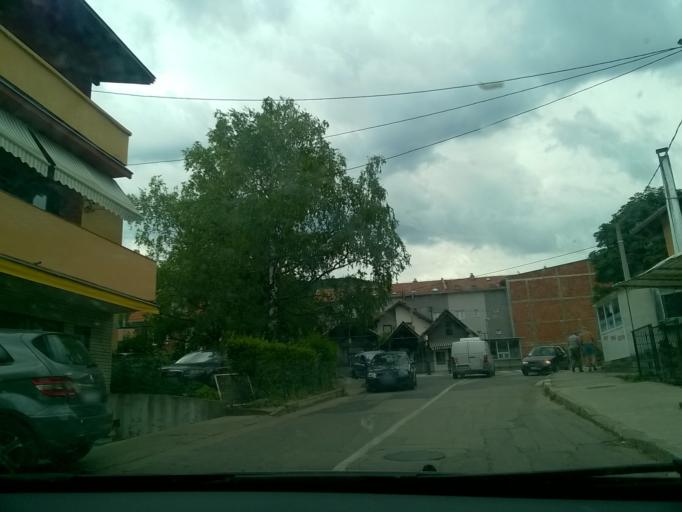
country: RS
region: Central Serbia
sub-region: Zajecarski Okrug
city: Soko Banja
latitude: 43.6457
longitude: 21.8753
